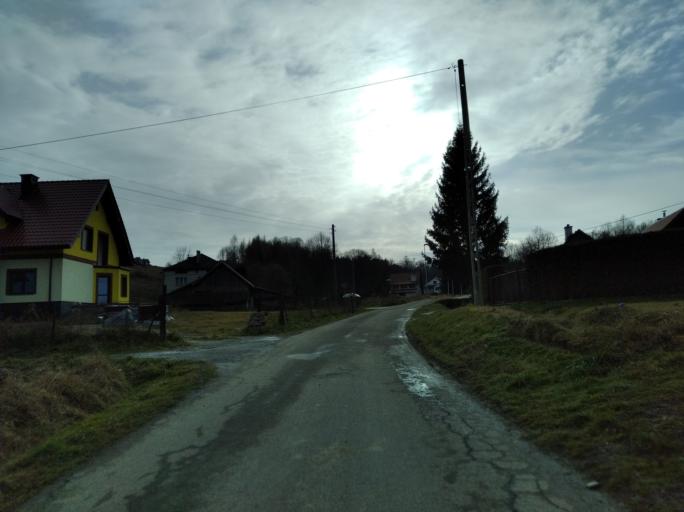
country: PL
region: Subcarpathian Voivodeship
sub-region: Powiat strzyzowski
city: Strzyzow
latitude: 49.8613
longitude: 21.7827
